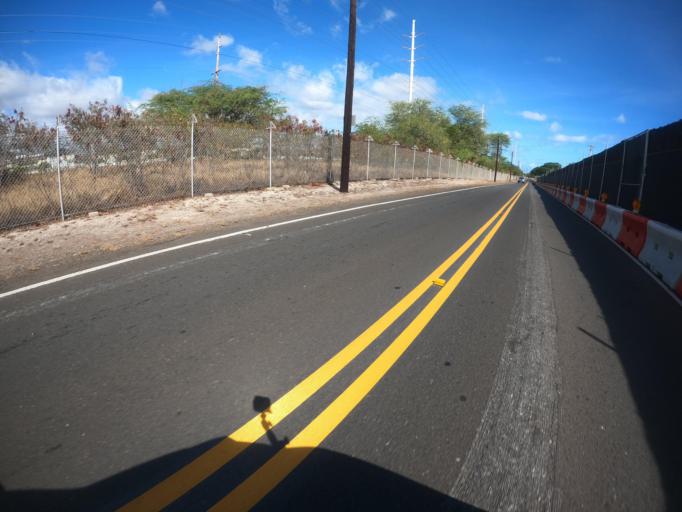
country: US
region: Hawaii
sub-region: Honolulu County
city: Makakilo City
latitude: 21.3245
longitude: -158.0836
